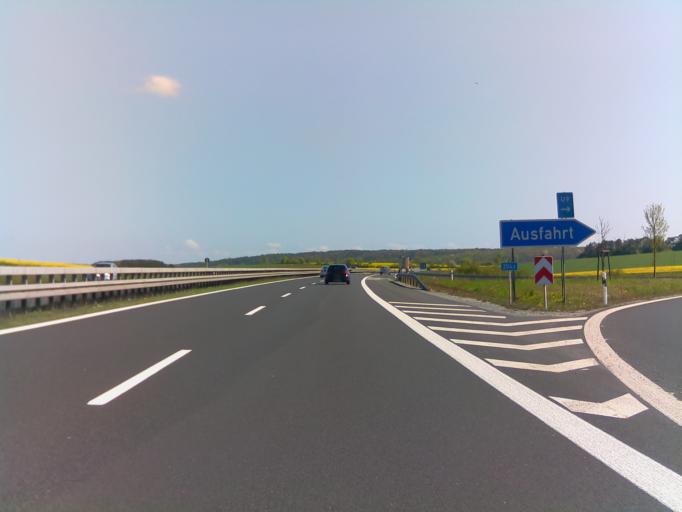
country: DE
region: Bavaria
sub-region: Regierungsbezirk Unterfranken
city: Oerlenbach
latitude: 50.1407
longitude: 10.1538
